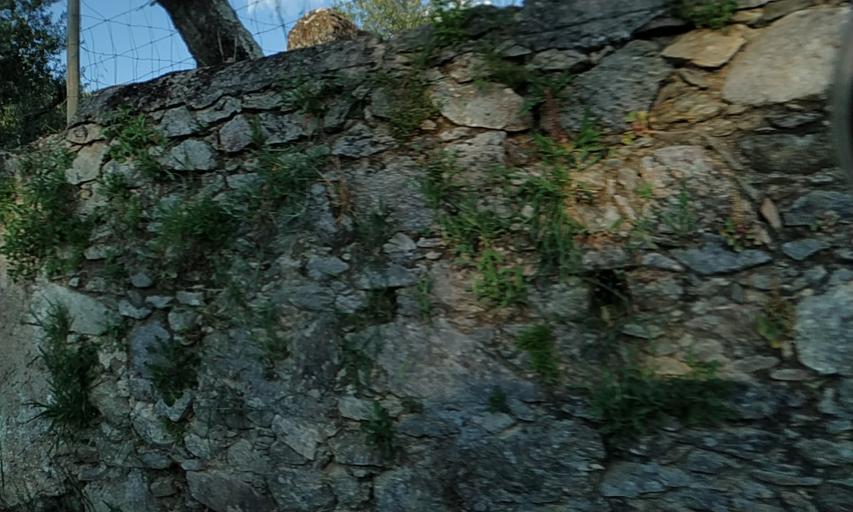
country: PT
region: Portalegre
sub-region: Portalegre
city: Portalegre
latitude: 39.3162
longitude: -7.4400
